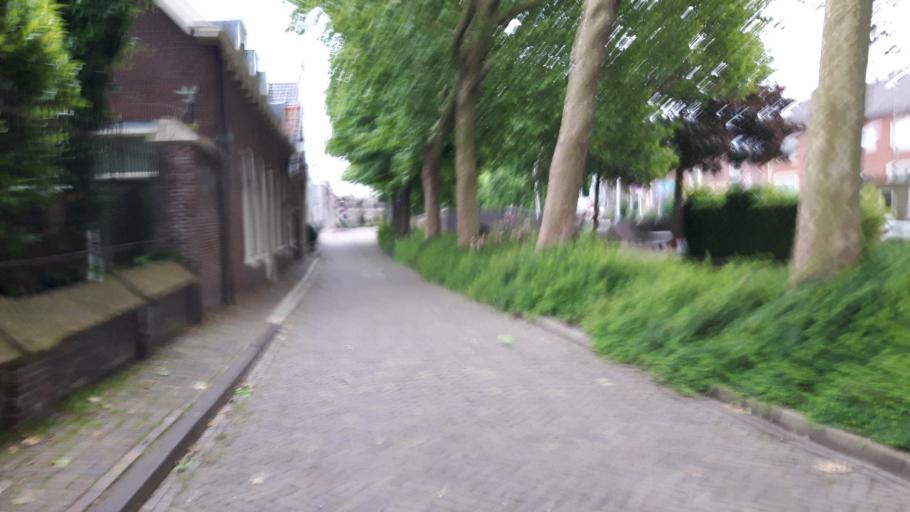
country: NL
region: Utrecht
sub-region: Gemeente Oudewater
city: Oudewater
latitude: 52.0250
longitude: 4.8704
